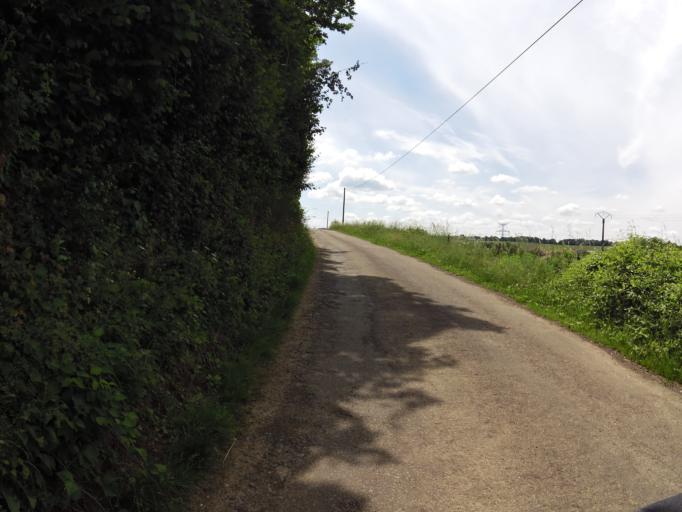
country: FR
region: Champagne-Ardenne
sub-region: Departement des Ardennes
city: Mouzon
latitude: 49.5237
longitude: 5.0934
